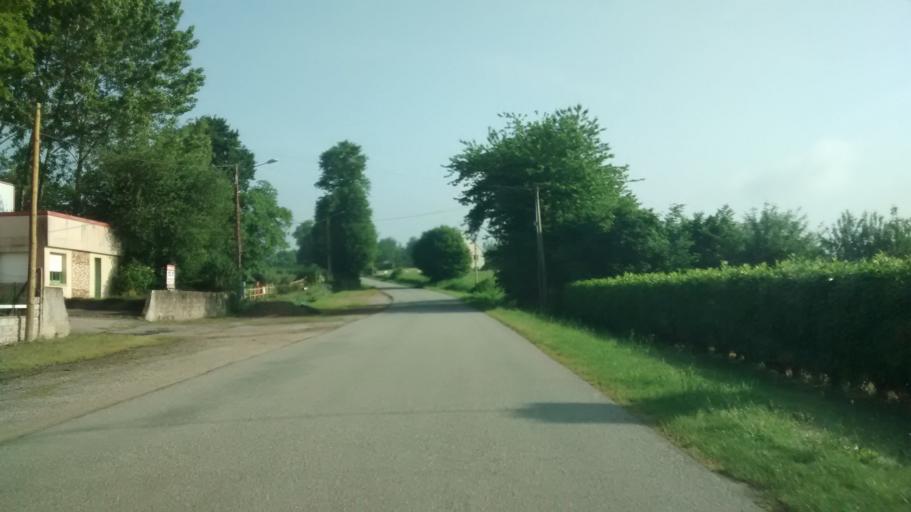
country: FR
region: Brittany
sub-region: Departement du Morbihan
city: Ruffiac
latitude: 47.8222
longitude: -2.2825
